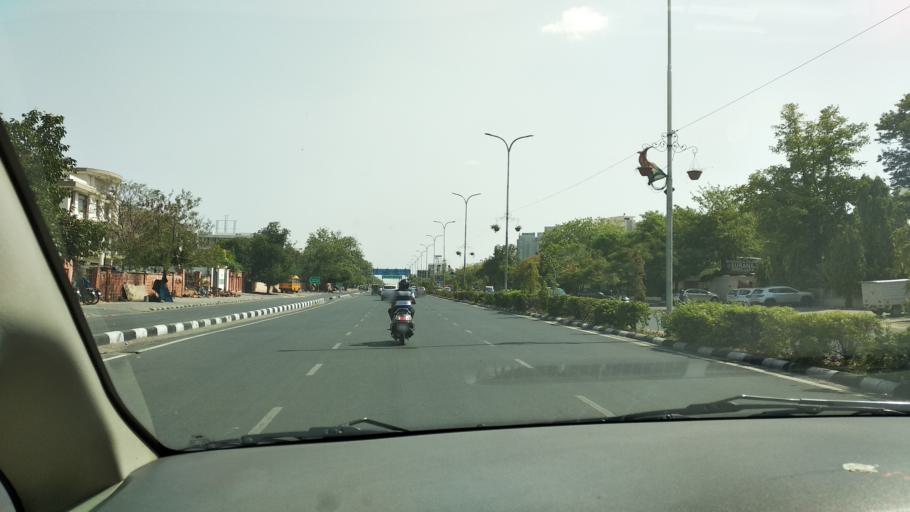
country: IN
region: Rajasthan
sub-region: Jaipur
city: Jaipur
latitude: 26.8979
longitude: 75.8160
